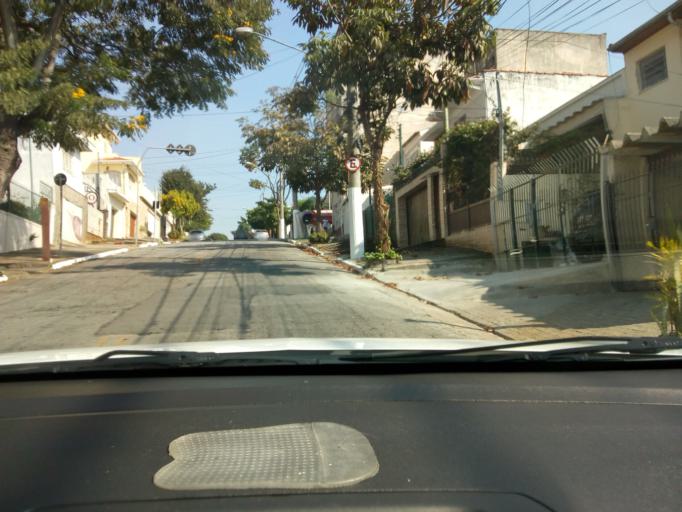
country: BR
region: Sao Paulo
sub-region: Sao Paulo
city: Sao Paulo
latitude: -23.5845
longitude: -46.6238
